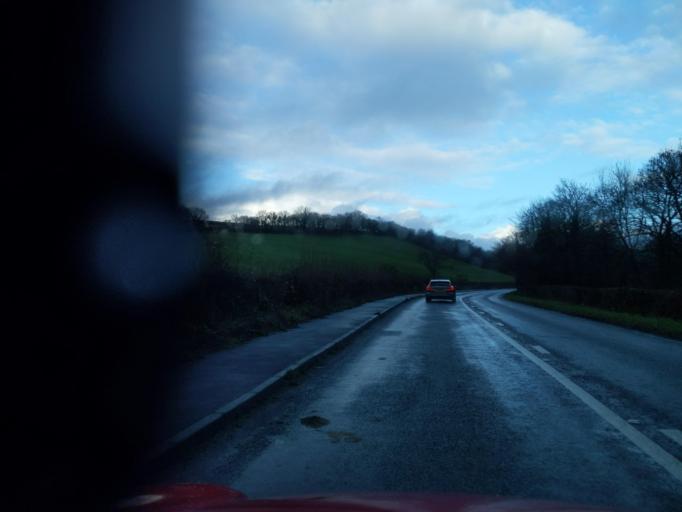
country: GB
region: England
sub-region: Devon
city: Tavistock
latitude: 50.5648
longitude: -4.1247
